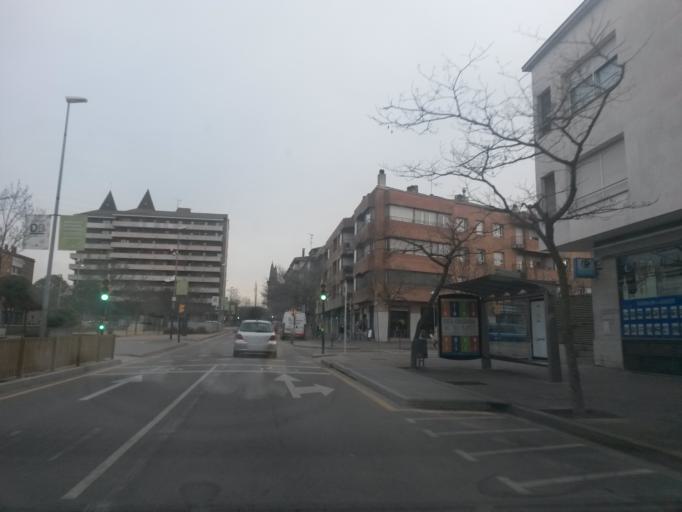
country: ES
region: Catalonia
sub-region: Provincia de Girona
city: Girona
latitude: 41.9826
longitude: 2.8139
